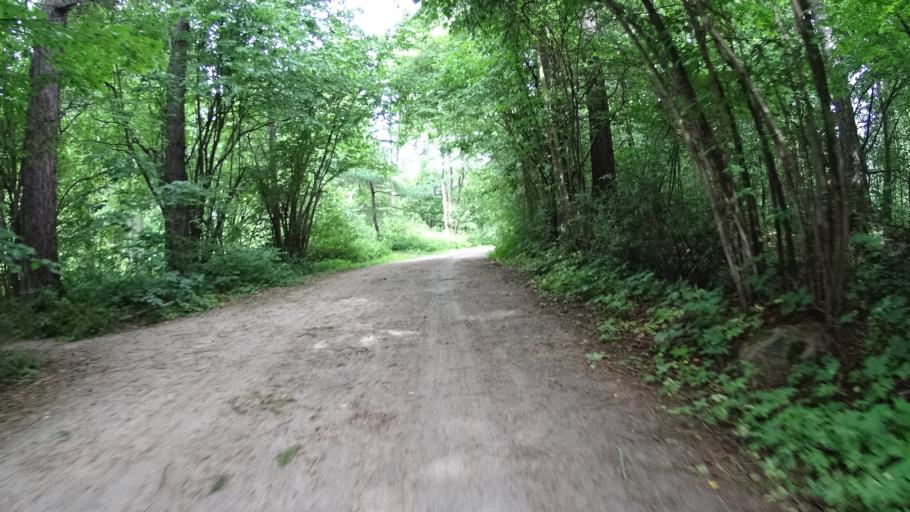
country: FI
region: Uusimaa
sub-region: Helsinki
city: Helsinki
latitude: 60.2729
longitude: 24.9327
